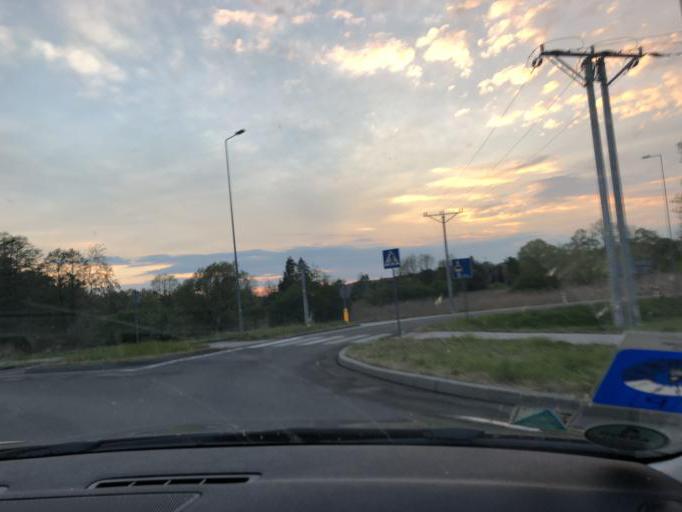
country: PL
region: Lubusz
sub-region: Powiat zarski
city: Trzebiel
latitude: 51.6330
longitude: 14.8156
